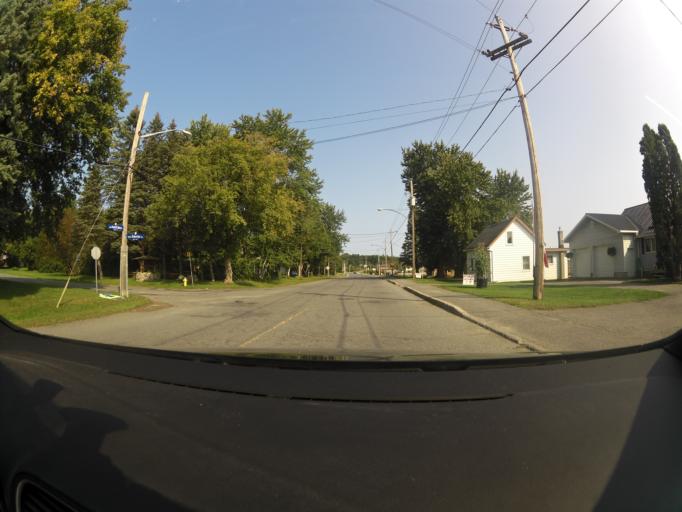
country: CA
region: Ontario
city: Bells Corners
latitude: 45.3449
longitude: -76.0269
